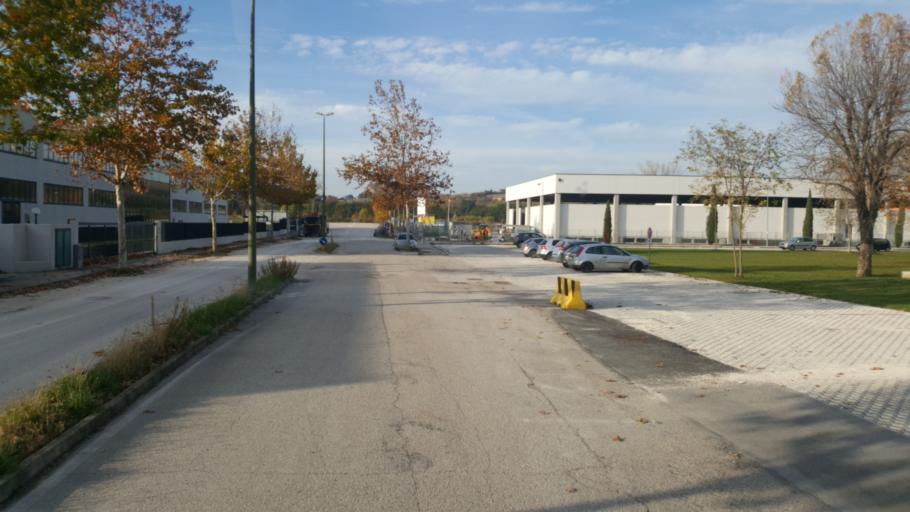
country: IT
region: The Marches
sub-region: Provincia di Ancona
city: Casine
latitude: 43.6478
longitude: 13.1396
